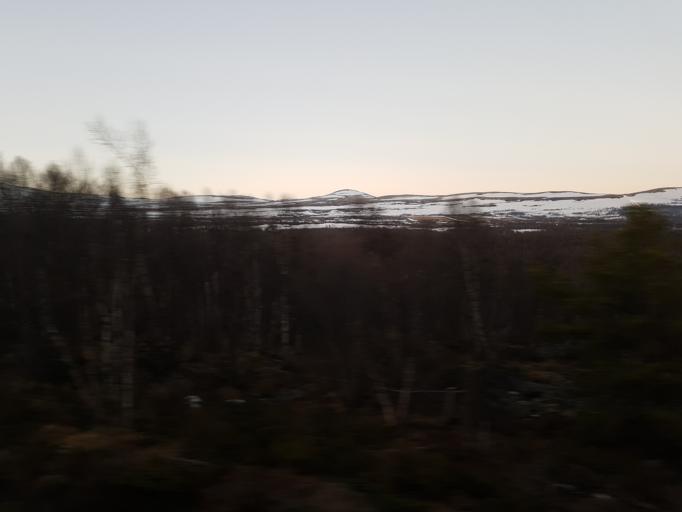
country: NO
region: Oppland
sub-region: Dovre
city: Dombas
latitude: 62.1014
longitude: 9.2038
